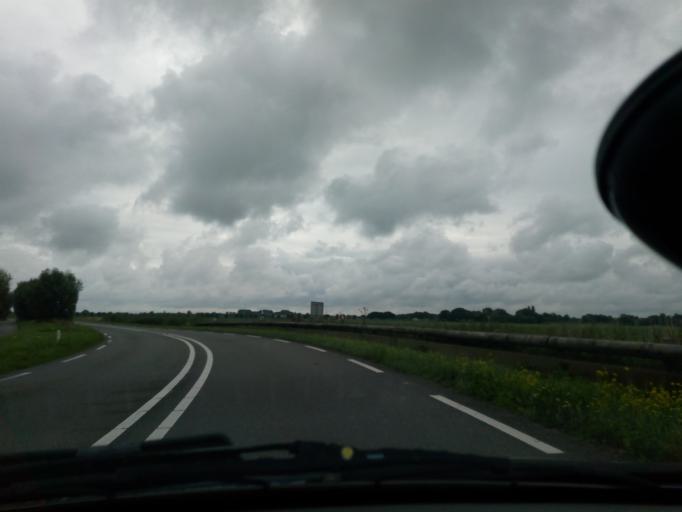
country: NL
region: South Holland
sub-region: Gemeente Alphen aan den Rijn
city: Alphen aan den Rijn
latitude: 52.1685
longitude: 4.6868
